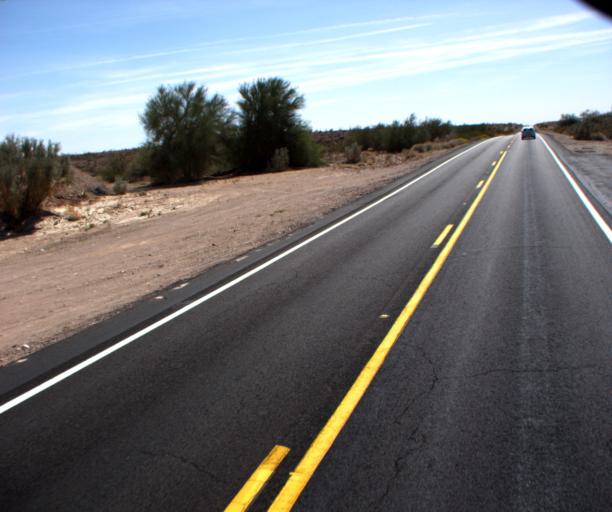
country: US
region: Arizona
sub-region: La Paz County
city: Quartzsite
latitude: 33.1662
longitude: -114.2780
